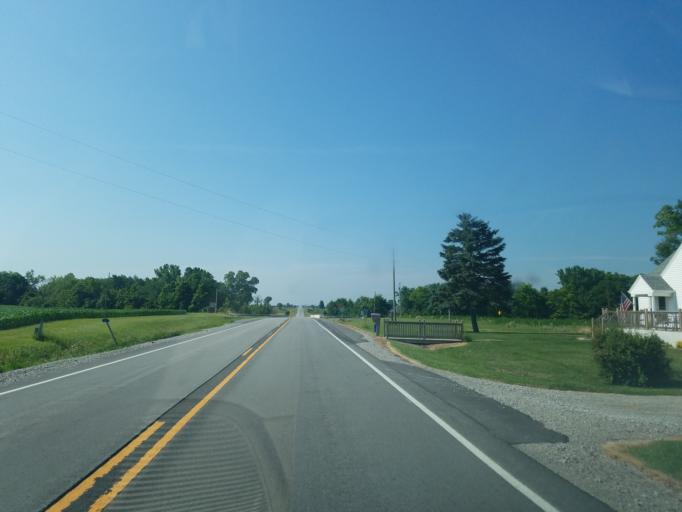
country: US
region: Indiana
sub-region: Allen County
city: Woodburn
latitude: 41.1718
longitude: -84.8492
